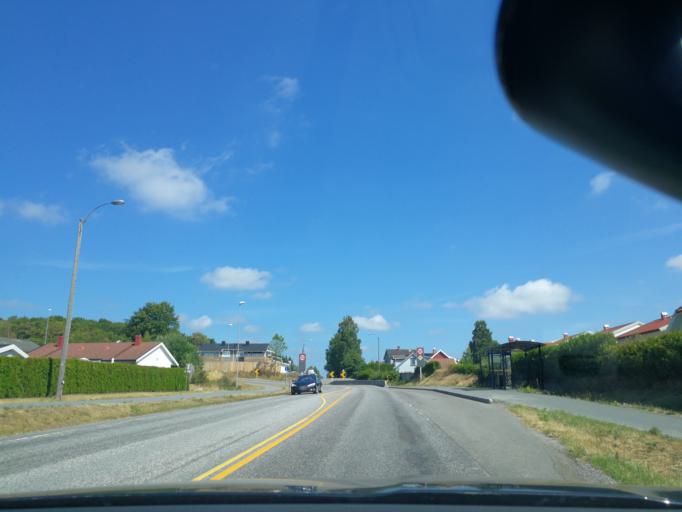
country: NO
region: Vestfold
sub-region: Sandefjord
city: Sandefjord
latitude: 59.1725
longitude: 10.2116
